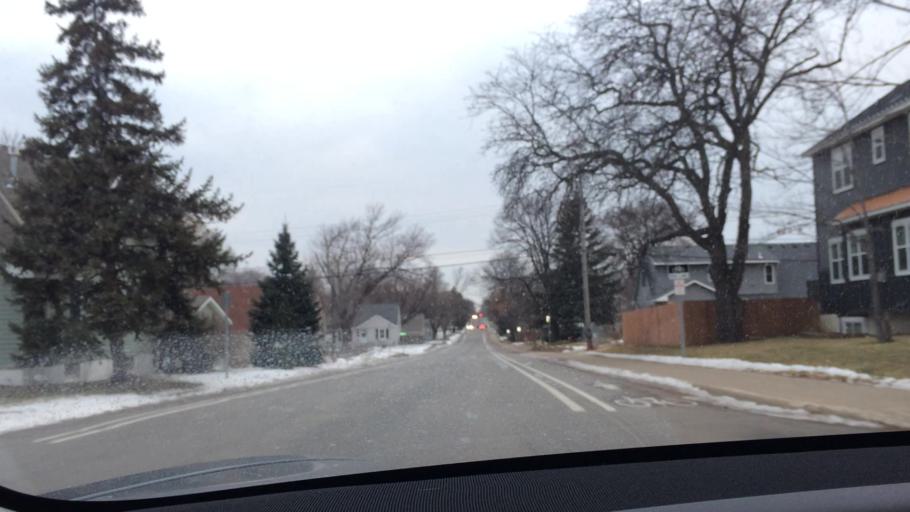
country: US
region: Minnesota
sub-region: Hennepin County
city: Saint Louis Park
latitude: 44.9532
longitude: -93.3658
